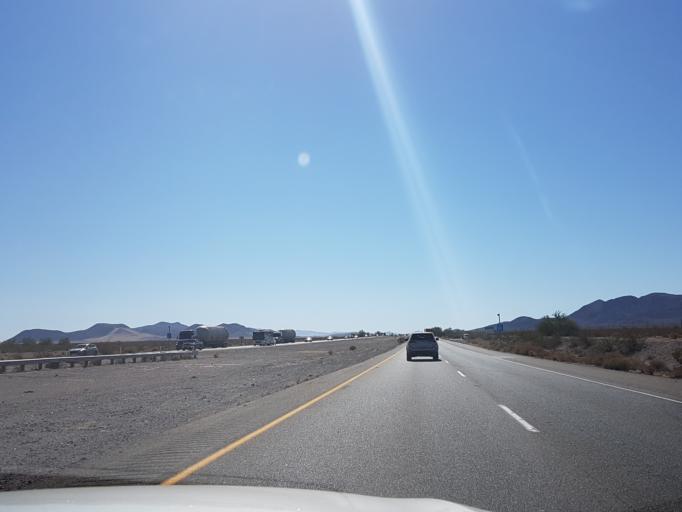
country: US
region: California
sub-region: San Bernardino County
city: Fort Irwin
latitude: 35.1789
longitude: -116.1702
